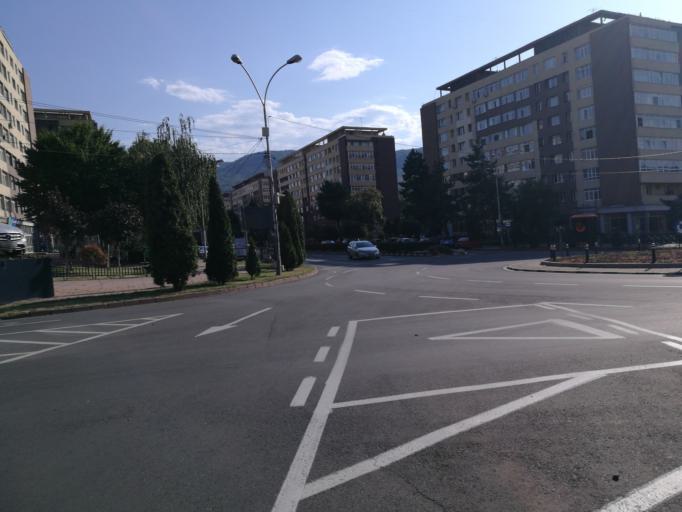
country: RO
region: Neamt
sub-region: Municipiul Piatra-Neamt
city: Valeni
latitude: 46.9317
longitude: 26.3711
